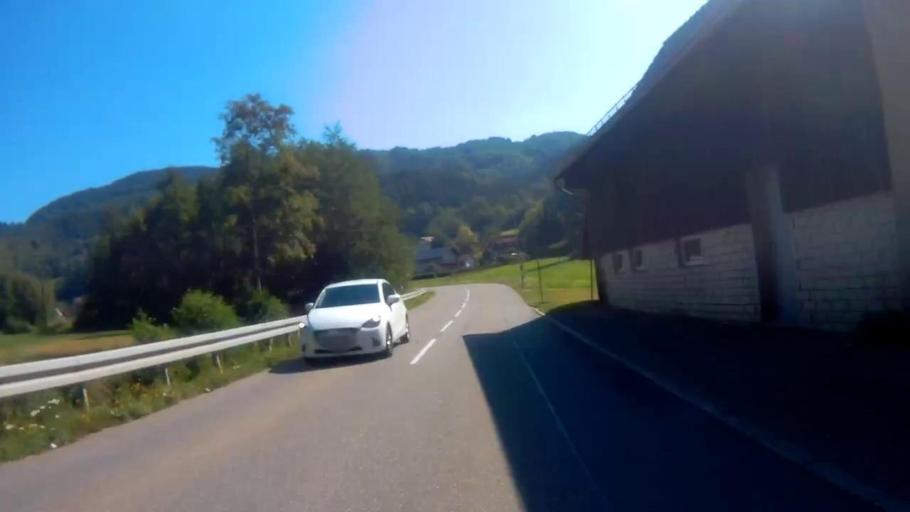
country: DE
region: Baden-Wuerttemberg
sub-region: Freiburg Region
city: Hausen
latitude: 47.7006
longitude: 7.7977
